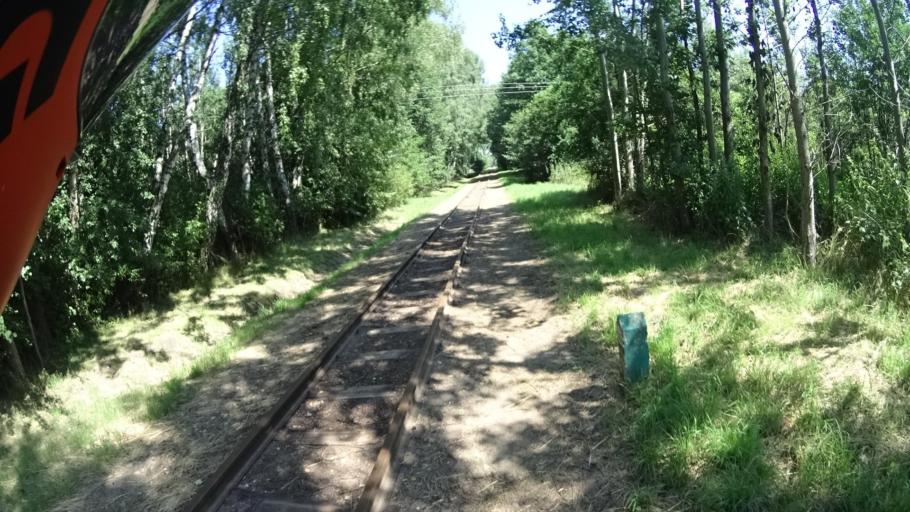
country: PL
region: Masovian Voivodeship
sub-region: Powiat piaseczynski
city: Tarczyn
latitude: 51.9829
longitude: 20.8768
